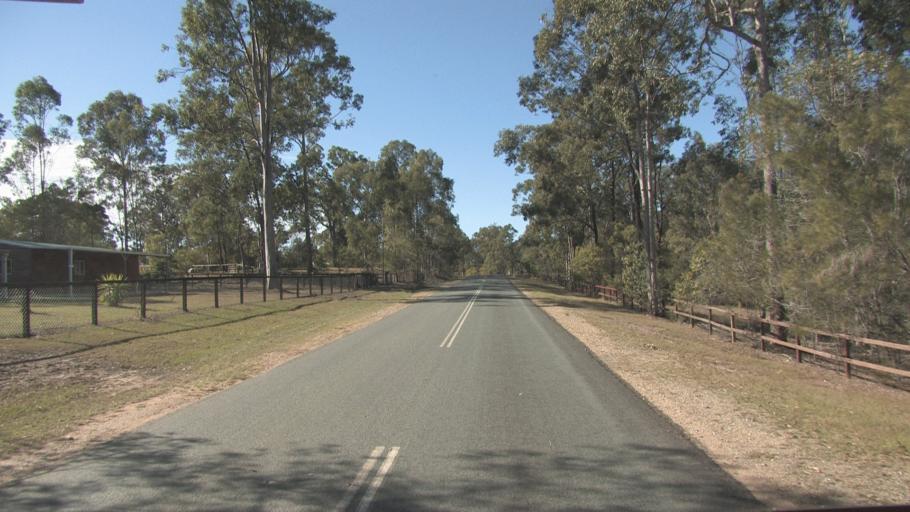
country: AU
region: Queensland
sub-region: Ipswich
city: Springfield Lakes
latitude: -27.7109
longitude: 152.9310
